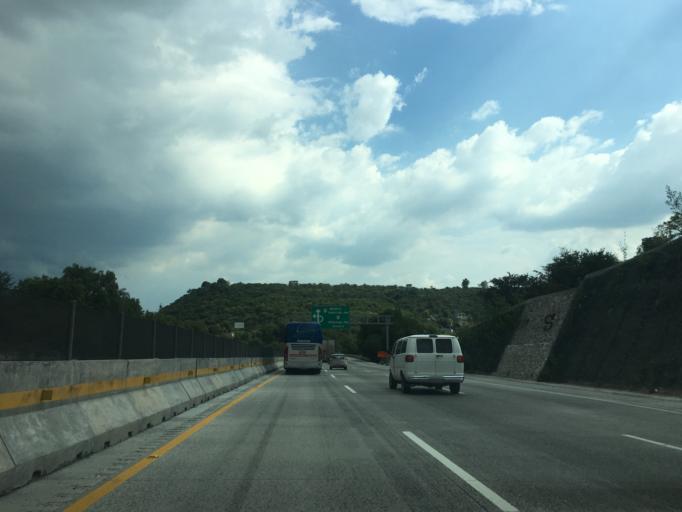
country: MX
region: Hidalgo
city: Tepeji de Ocampo
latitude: 19.9030
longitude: -99.3499
